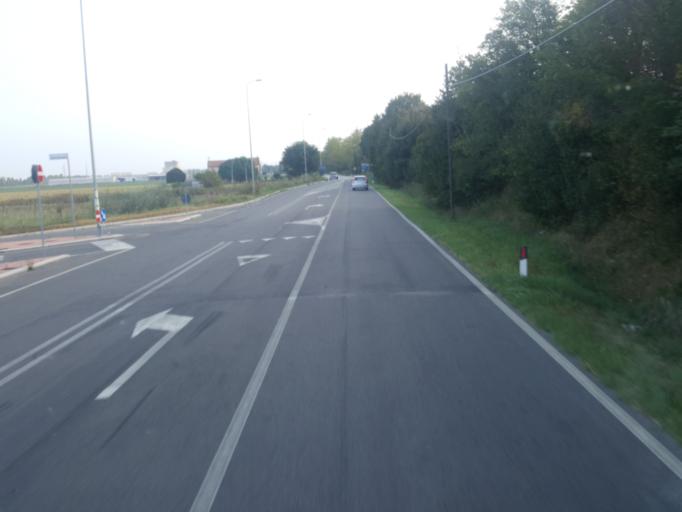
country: IT
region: Emilia-Romagna
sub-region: Provincia di Ravenna
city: Conselice
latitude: 44.5218
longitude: 11.8329
